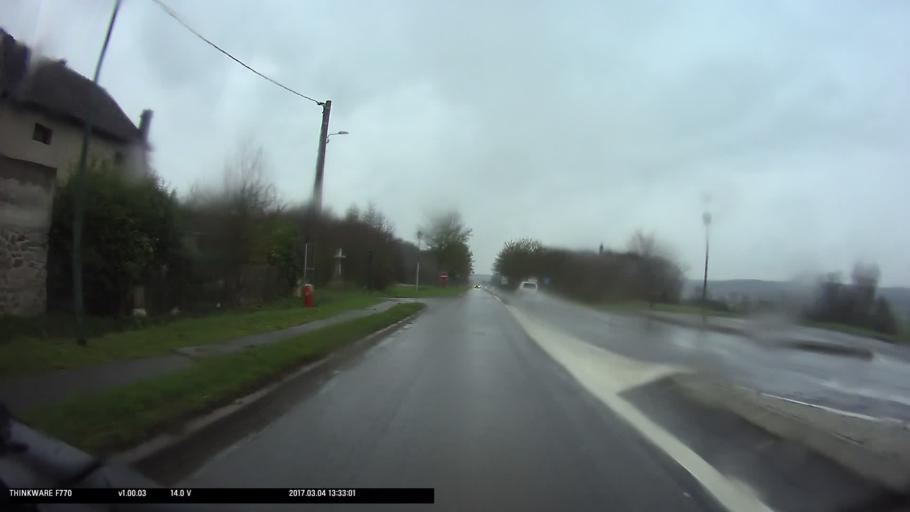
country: FR
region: Ile-de-France
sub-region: Departement du Val-d'Oise
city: Marines
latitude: 49.1277
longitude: 1.9978
